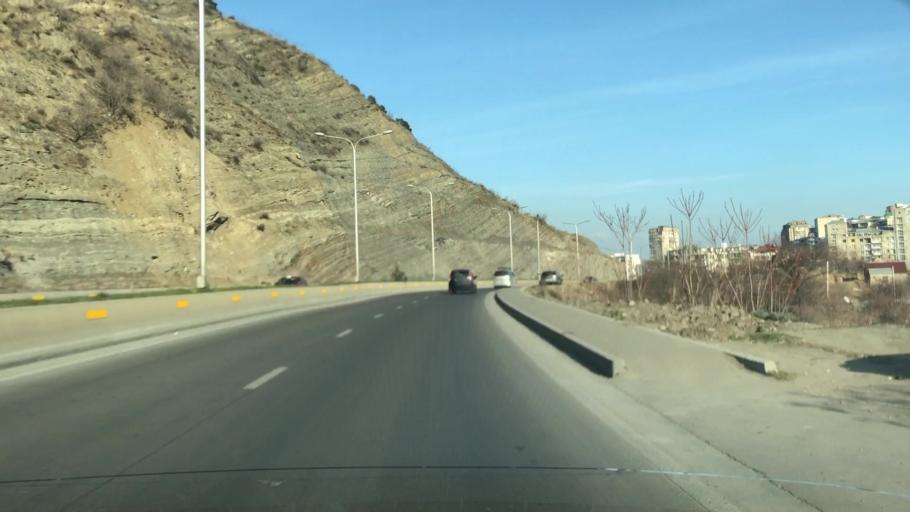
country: GE
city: Tsqnet'i
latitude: 41.7159
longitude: 44.7502
